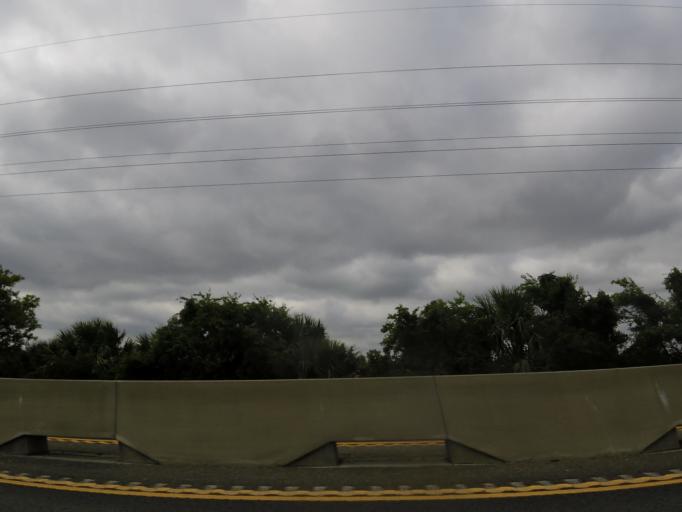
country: US
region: Georgia
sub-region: Glynn County
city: Brunswick
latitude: 31.1619
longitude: -81.4658
